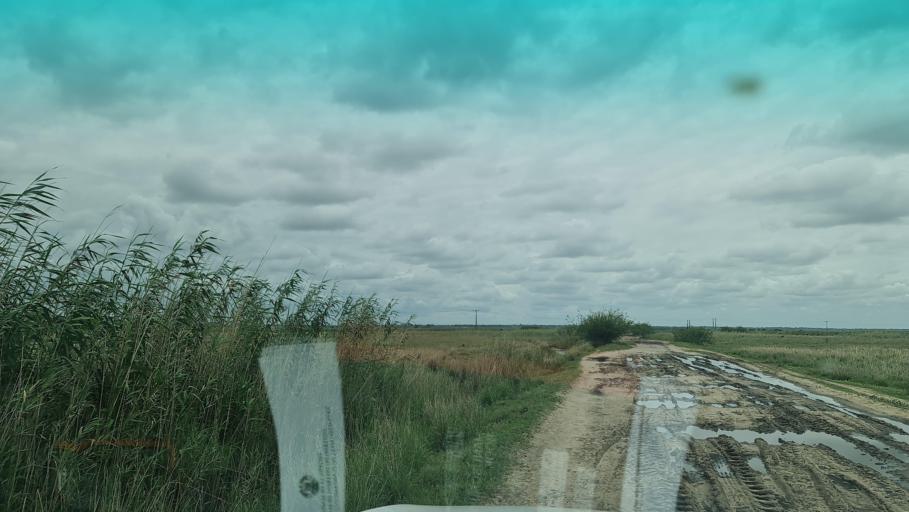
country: MZ
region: Maputo City
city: Maputo
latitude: -25.7262
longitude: 32.7015
